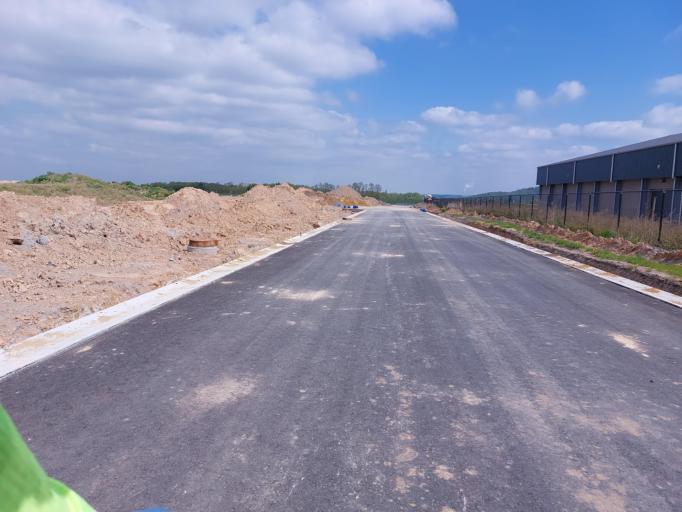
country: BE
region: Wallonia
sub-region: Province du Hainaut
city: Frameries
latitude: 50.4175
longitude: 3.9121
